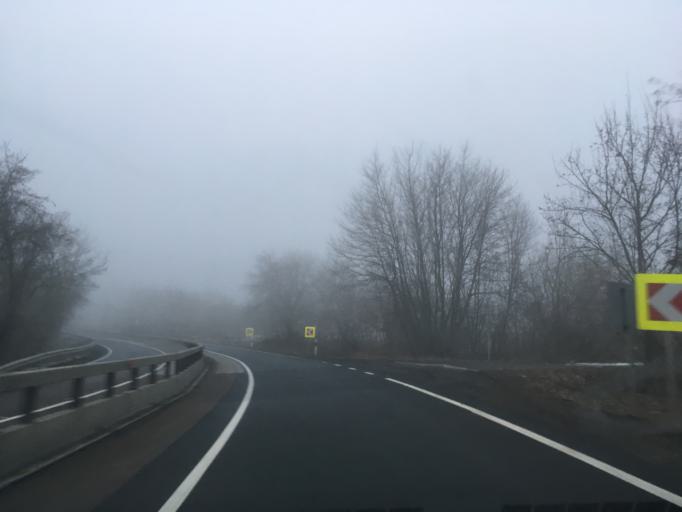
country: HU
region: Heves
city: Egerszalok
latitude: 47.8575
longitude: 20.3680
